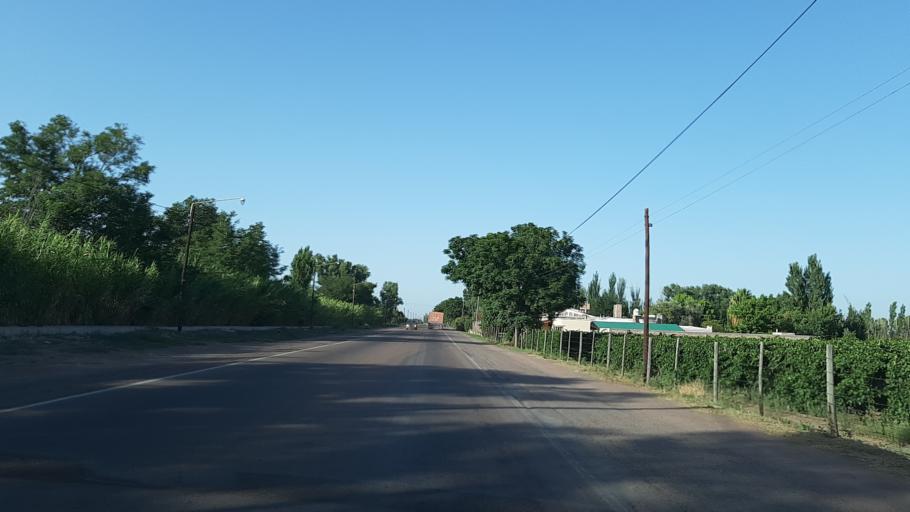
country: AR
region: Mendoza
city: San Martin
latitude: -32.9864
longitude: -68.4653
